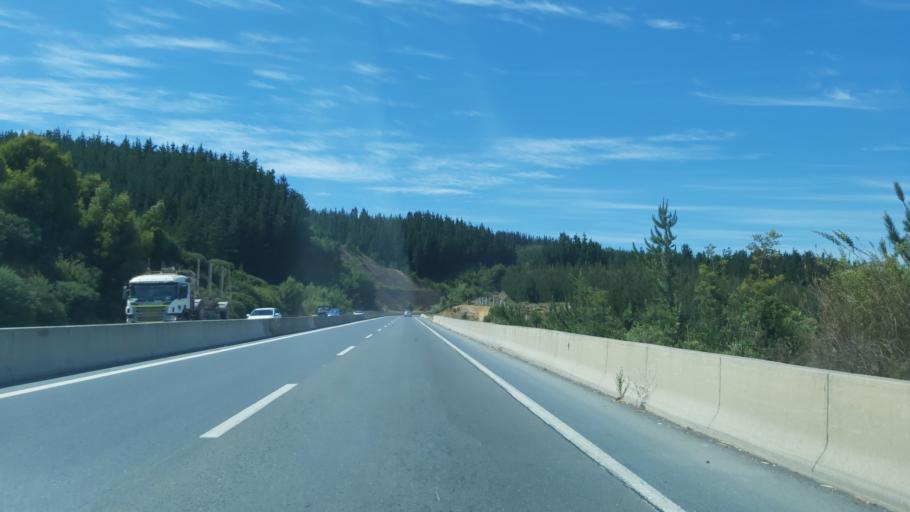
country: CL
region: Biobio
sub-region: Provincia de Concepcion
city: Lota
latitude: -37.0868
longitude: -73.1388
